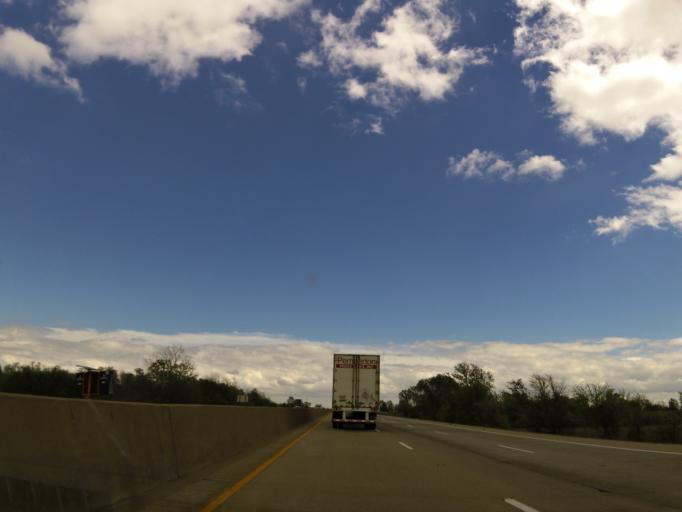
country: US
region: Arkansas
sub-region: Crittenden County
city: West Memphis
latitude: 35.1562
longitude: -90.1200
